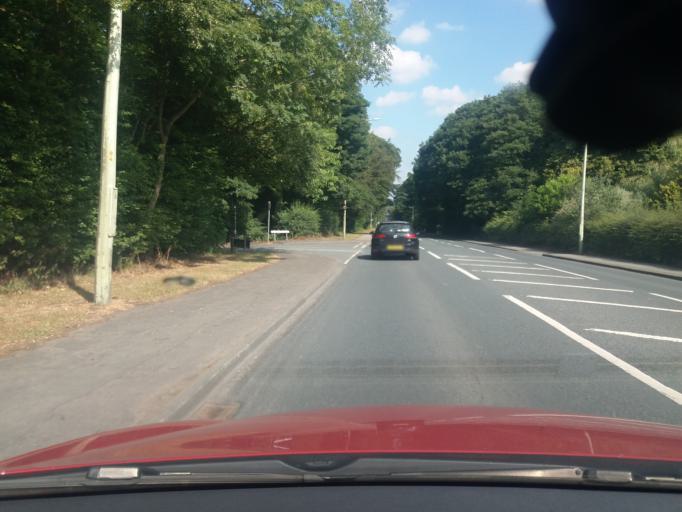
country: GB
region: England
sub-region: Lancashire
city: Chorley
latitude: 53.6350
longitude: -2.6146
